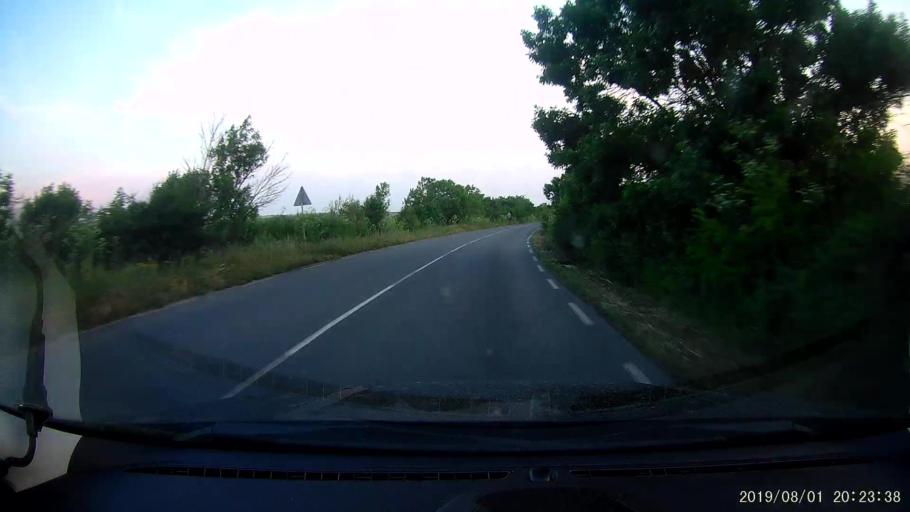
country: BG
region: Yambol
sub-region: Obshtina Elkhovo
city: Elkhovo
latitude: 42.2450
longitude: 26.5988
